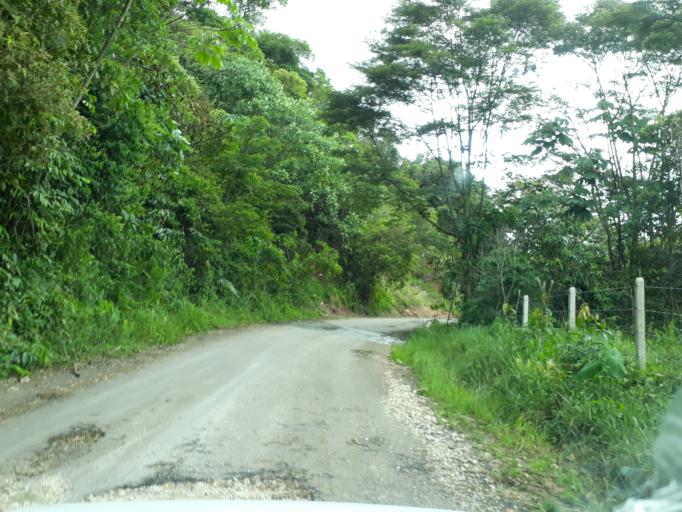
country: CO
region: Cundinamarca
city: Medina
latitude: 4.5768
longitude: -73.3489
